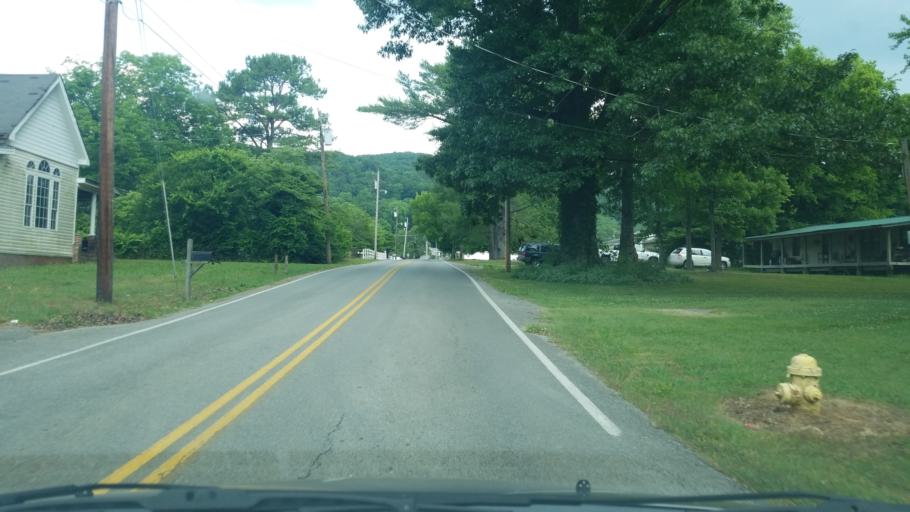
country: US
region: Tennessee
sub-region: Hamilton County
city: Soddy-Daisy
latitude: 35.2442
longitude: -85.1871
